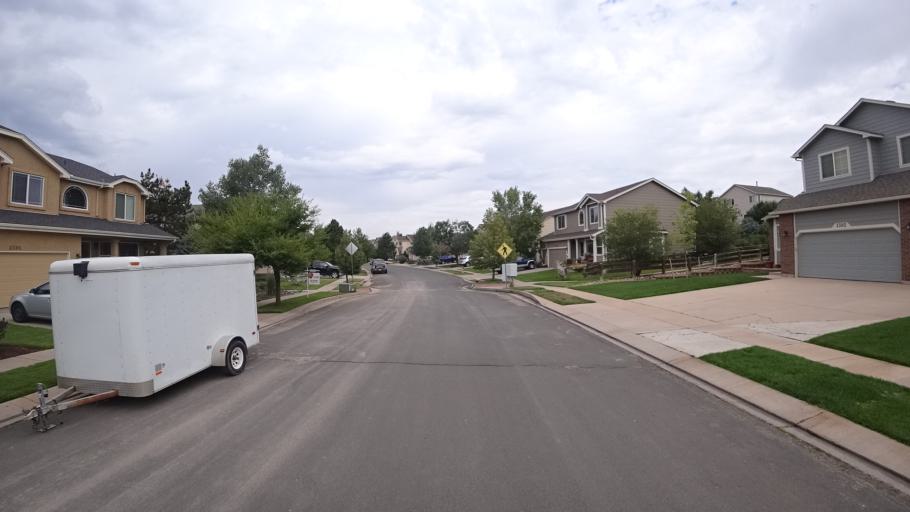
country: US
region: Colorado
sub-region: El Paso County
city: Gleneagle
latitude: 39.0056
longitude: -104.7993
